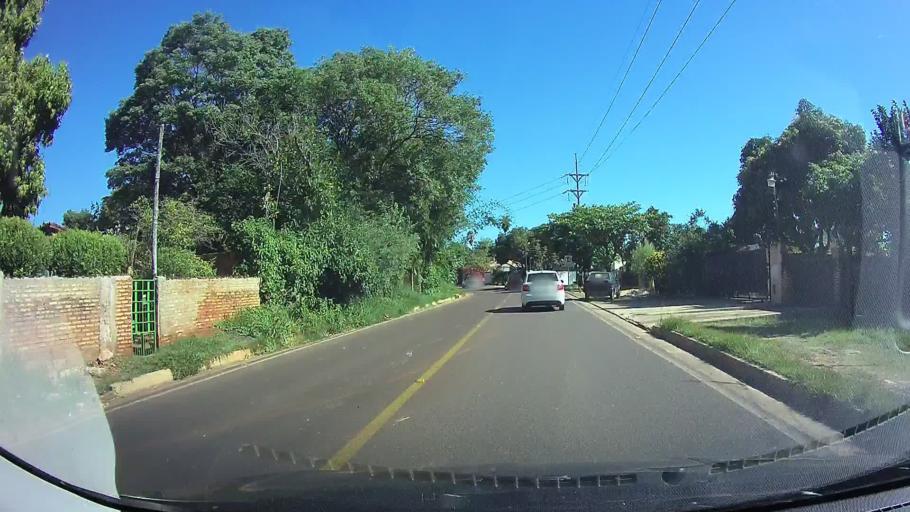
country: PY
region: Central
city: Fernando de la Mora
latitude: -25.3019
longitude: -57.5335
